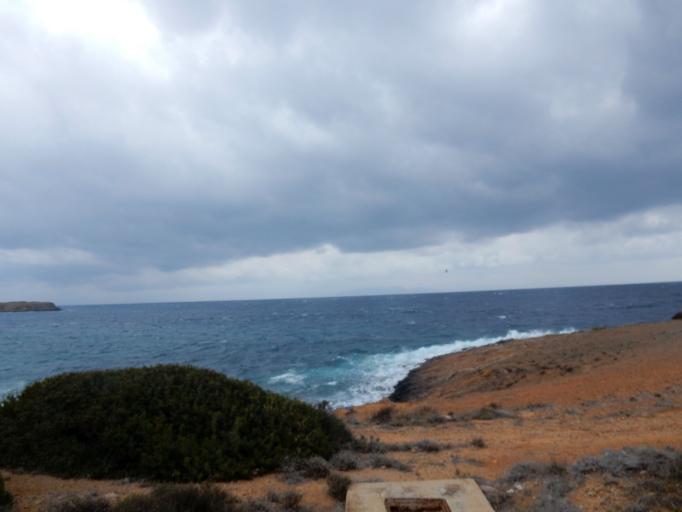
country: GR
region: Attica
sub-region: Nomarchia Anatolikis Attikis
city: Limin Mesoyaias
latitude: 37.9102
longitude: 24.0393
